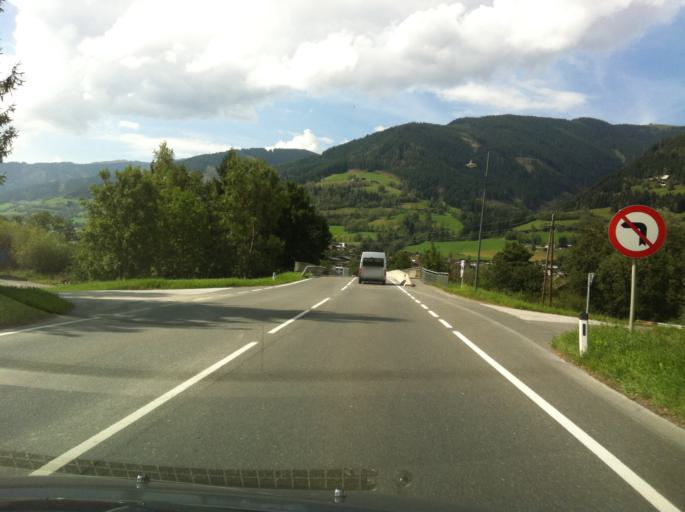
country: AT
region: Salzburg
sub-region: Politischer Bezirk Zell am See
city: Kaprun
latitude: 47.2837
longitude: 12.7528
